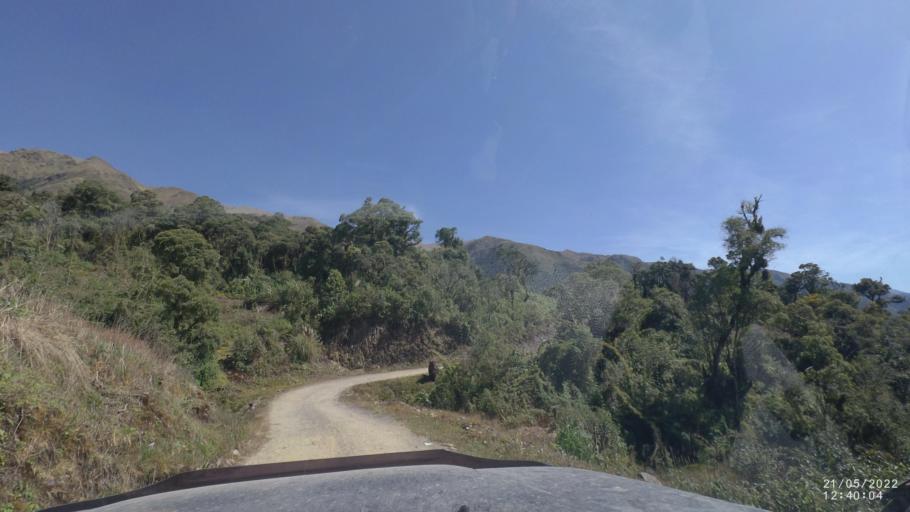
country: BO
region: Cochabamba
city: Colomi
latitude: -17.1974
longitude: -65.9249
